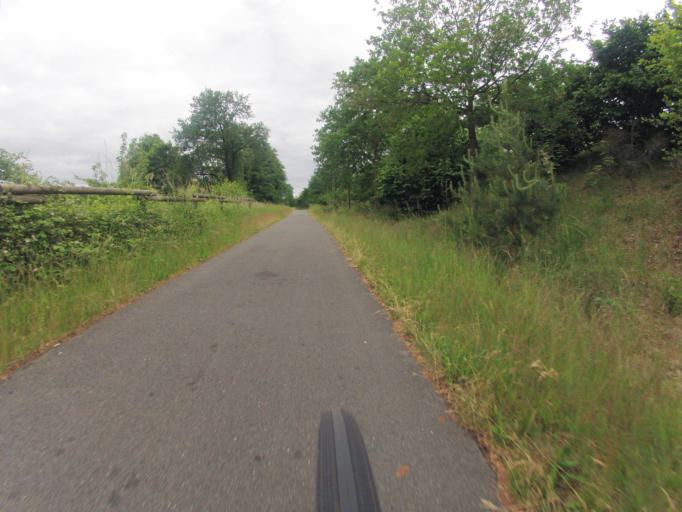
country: DE
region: North Rhine-Westphalia
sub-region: Regierungsbezirk Munster
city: Birgte
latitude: 52.2177
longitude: 7.6771
